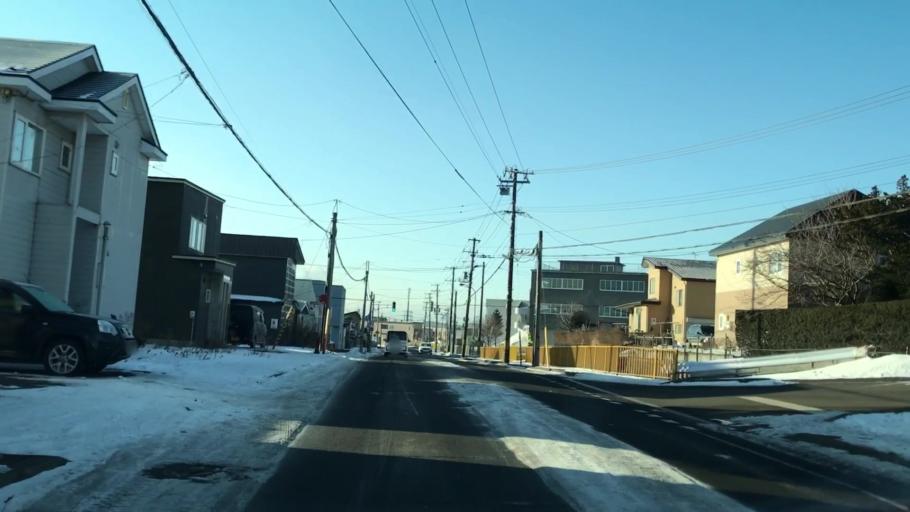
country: JP
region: Hokkaido
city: Muroran
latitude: 42.3672
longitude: 141.0496
